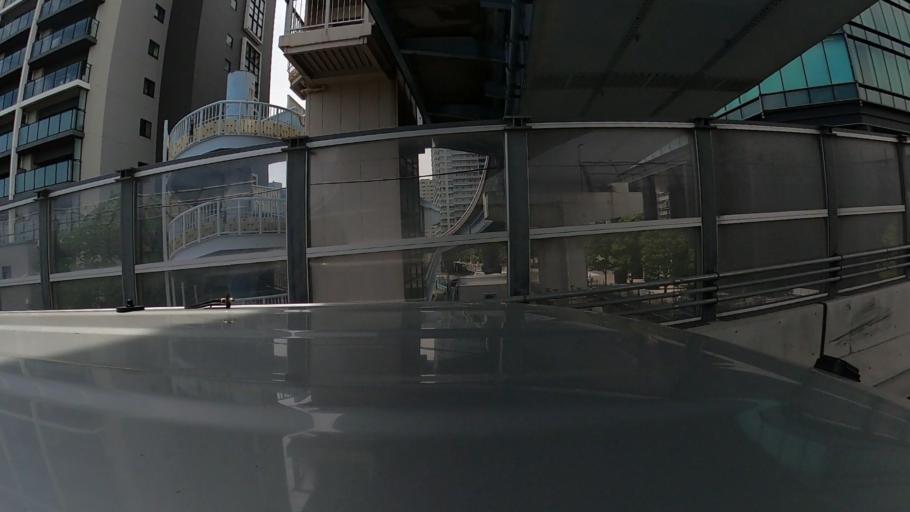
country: JP
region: Kanagawa
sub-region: Kawasaki-shi
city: Kawasaki
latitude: 35.6075
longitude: 139.7505
